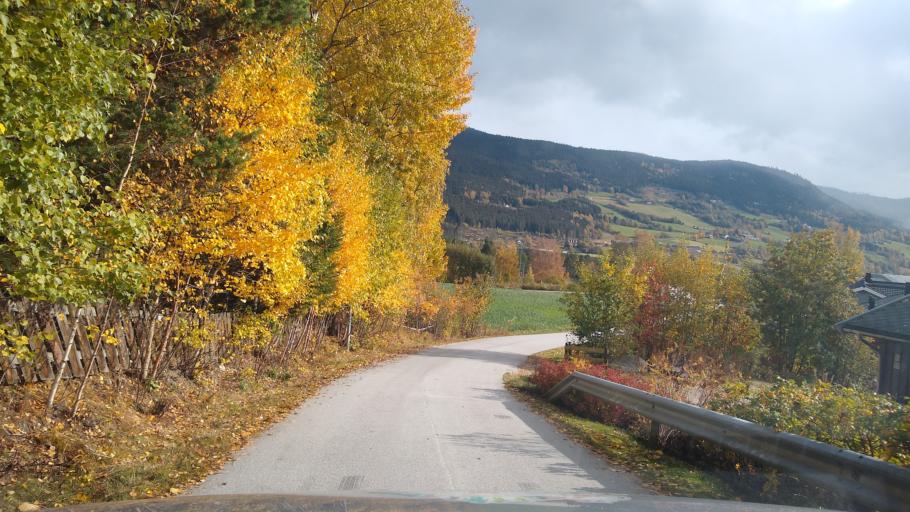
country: NO
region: Oppland
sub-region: Ringebu
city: Ringebu
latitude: 61.5404
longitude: 10.1284
